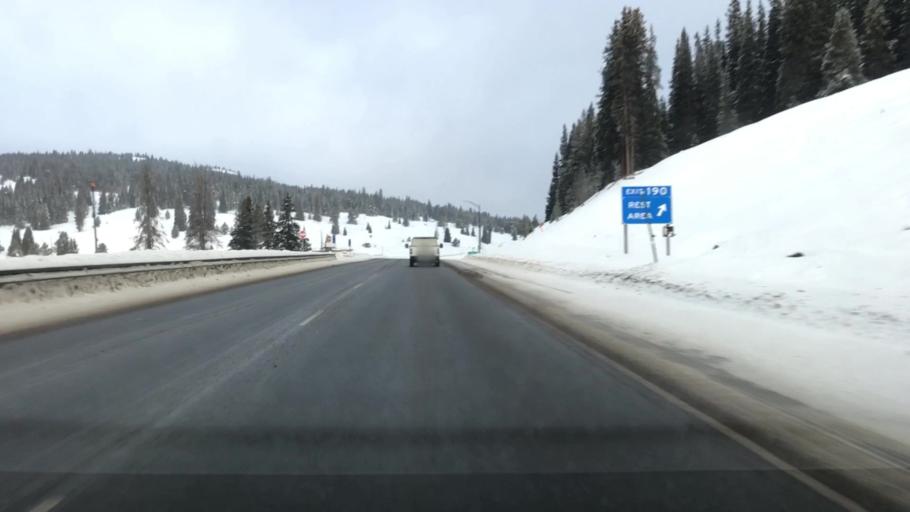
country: US
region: Colorado
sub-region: Summit County
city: Frisco
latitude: 39.5245
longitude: -106.2149
